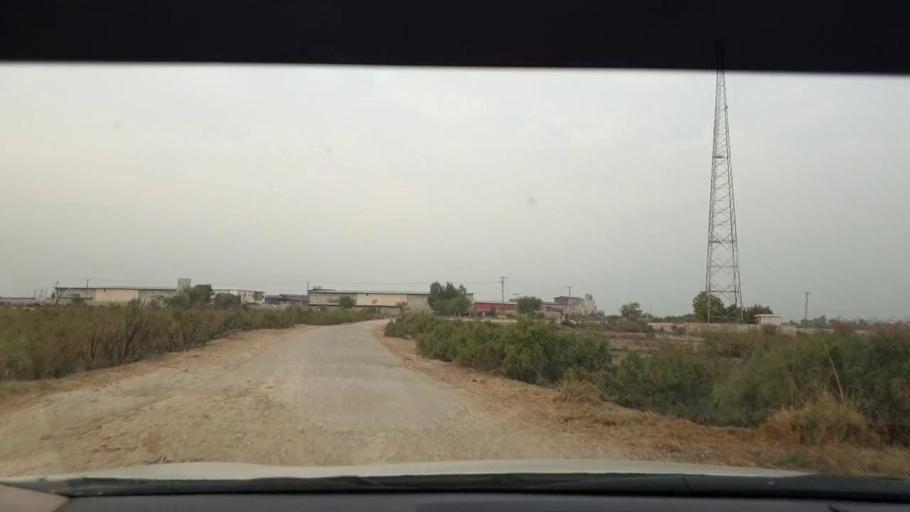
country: PK
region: Sindh
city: Sinjhoro
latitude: 25.9362
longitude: 68.7518
